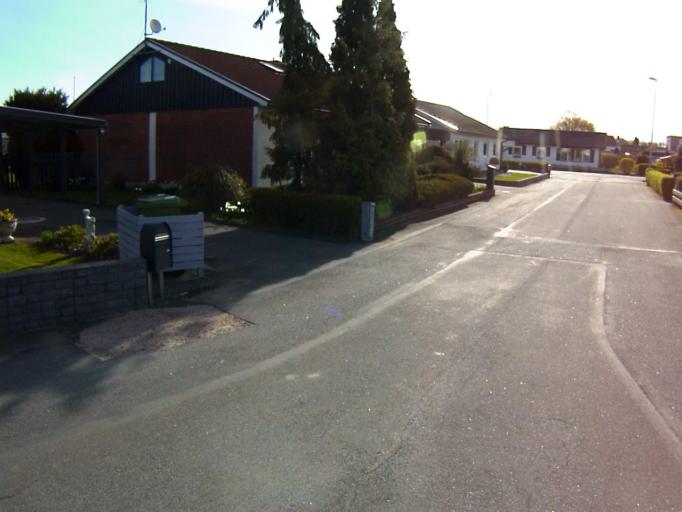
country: SE
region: Skane
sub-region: Kristianstads Kommun
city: Kristianstad
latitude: 56.0117
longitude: 14.1465
